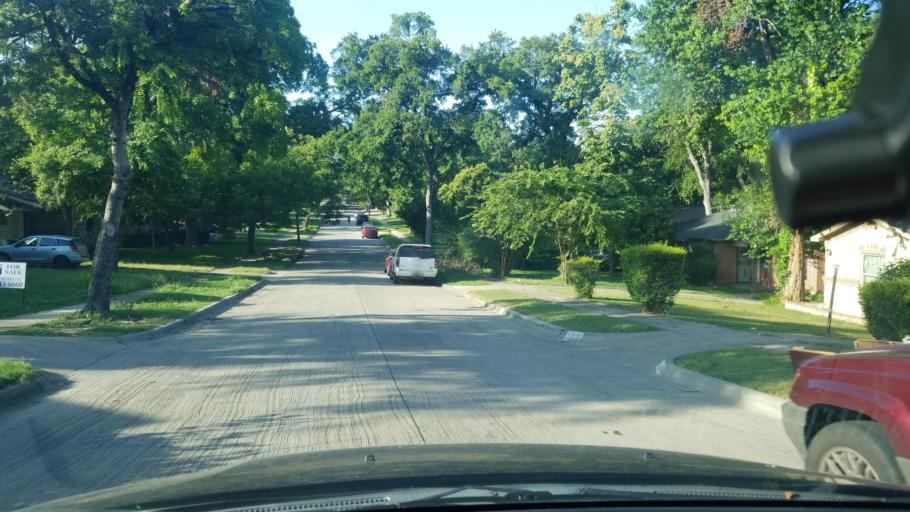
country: US
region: Texas
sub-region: Dallas County
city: Dallas
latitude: 32.7328
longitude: -96.8157
